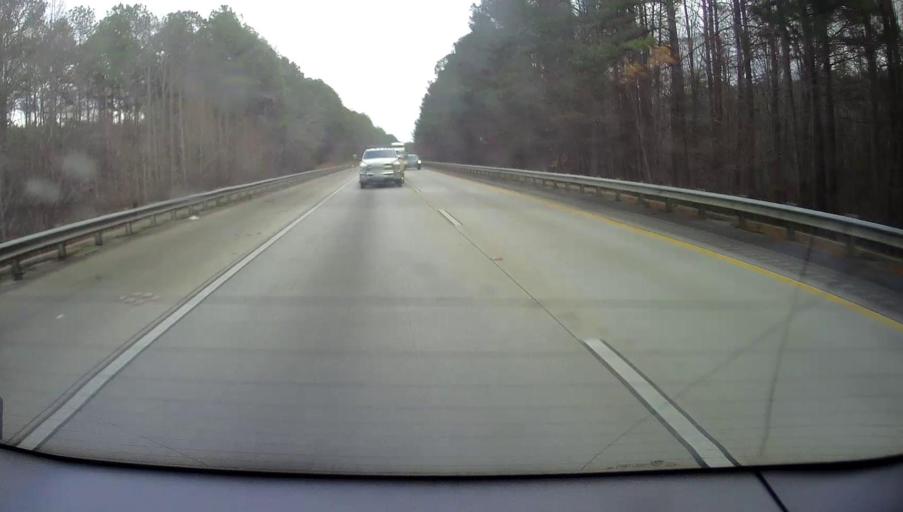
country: US
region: Georgia
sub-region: Carroll County
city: Mount Zion
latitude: 33.6896
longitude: -85.2137
